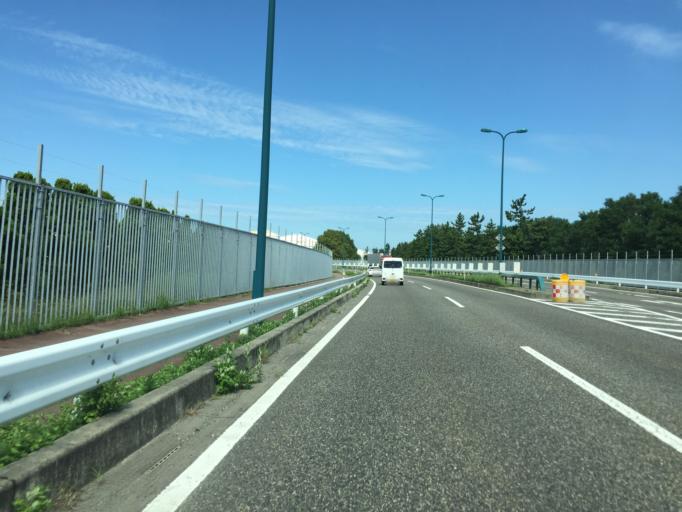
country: JP
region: Niigata
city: Niigata-shi
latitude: 37.9446
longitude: 139.0864
